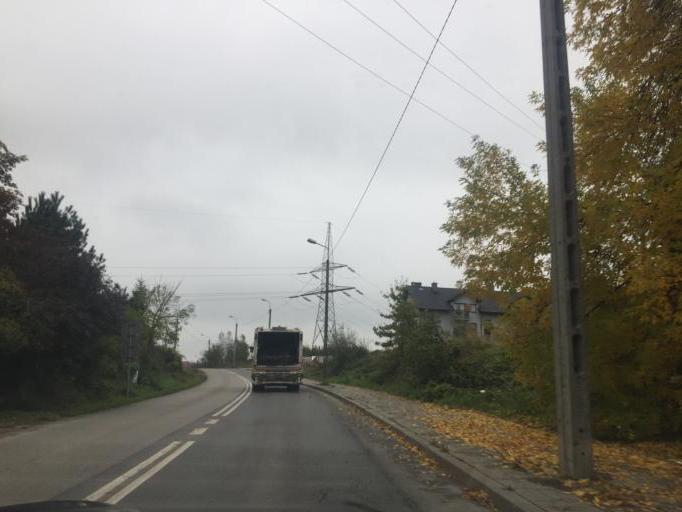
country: PL
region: Lesser Poland Voivodeship
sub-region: Powiat wielicki
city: Wieliczka
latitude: 49.9933
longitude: 20.0204
